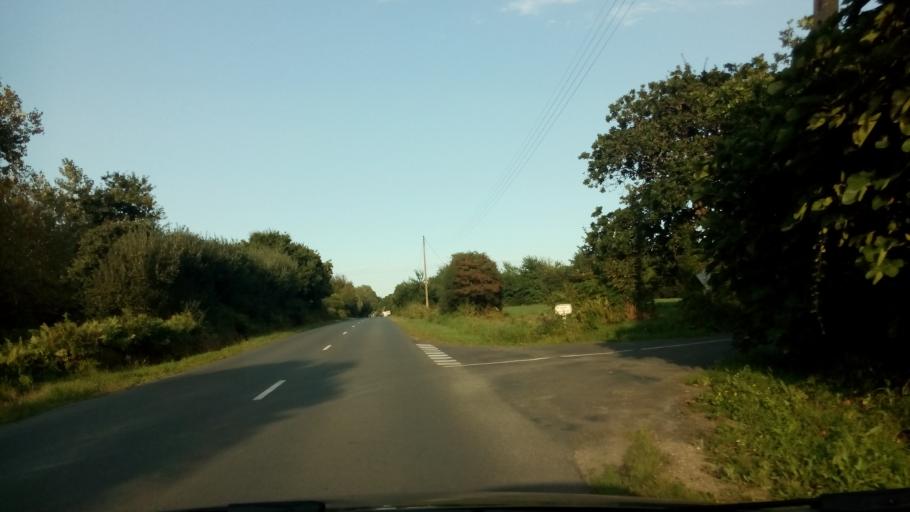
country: FR
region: Brittany
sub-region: Departement des Cotes-d'Armor
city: Trebeurden
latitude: 48.7903
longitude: -3.5659
